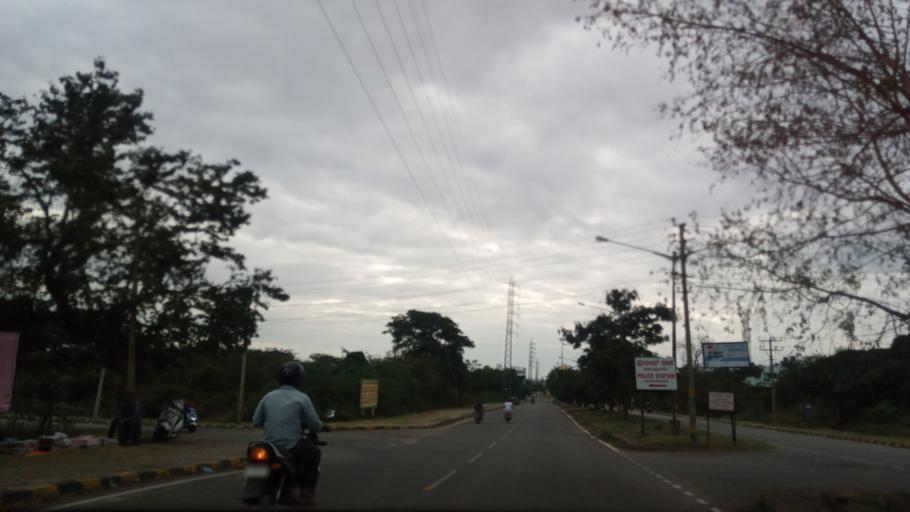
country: IN
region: Karnataka
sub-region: Mysore
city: Mysore
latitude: 12.2886
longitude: 76.6197
